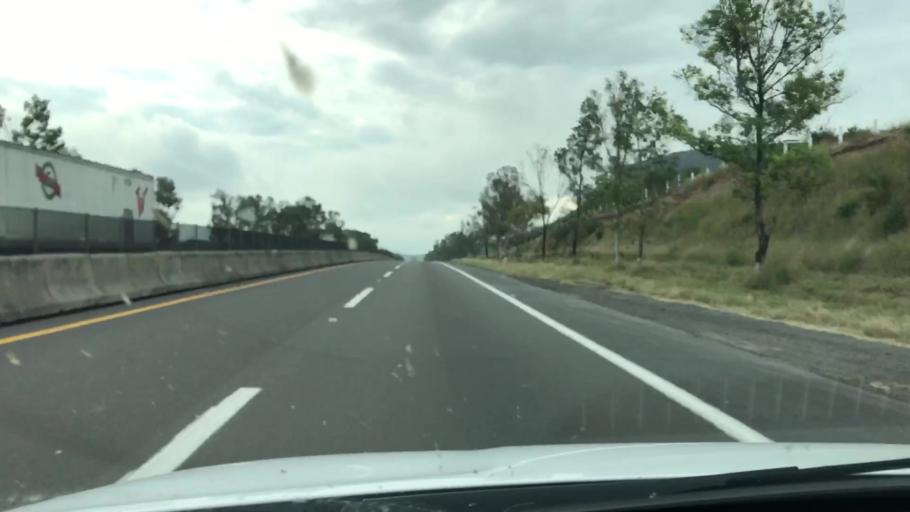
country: MX
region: Jalisco
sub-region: Lagos de Moreno
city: Cristeros [Fraccionamiento]
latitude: 21.2985
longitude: -102.0169
